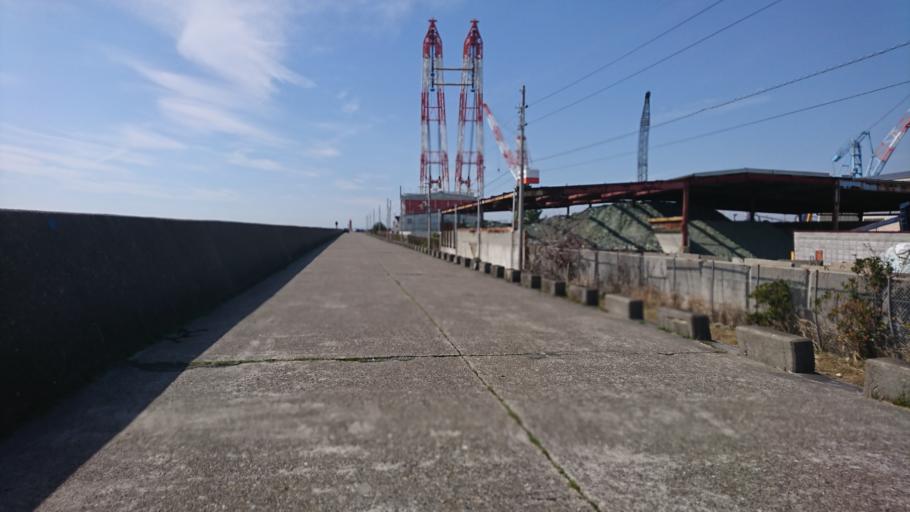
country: JP
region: Hyogo
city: Kakogawacho-honmachi
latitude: 34.6959
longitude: 134.8443
